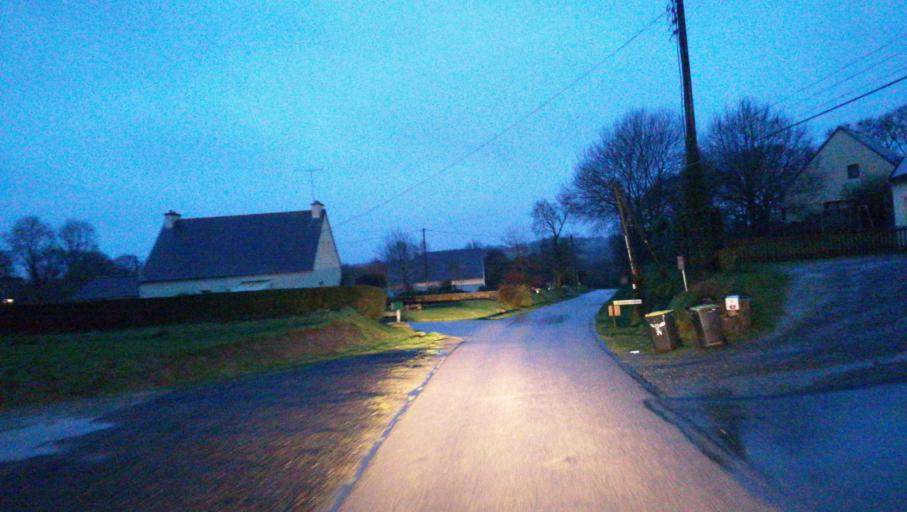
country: FR
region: Brittany
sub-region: Departement des Cotes-d'Armor
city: Plouagat
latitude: 48.4784
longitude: -2.9713
